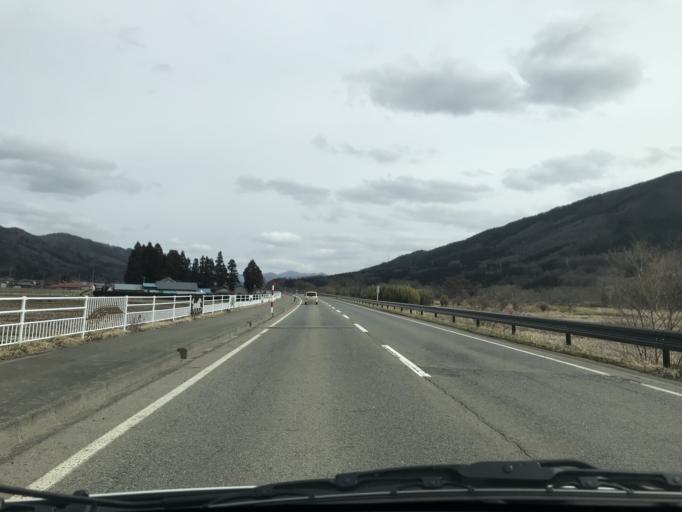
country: JP
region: Iwate
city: Tono
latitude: 39.3227
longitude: 141.4681
